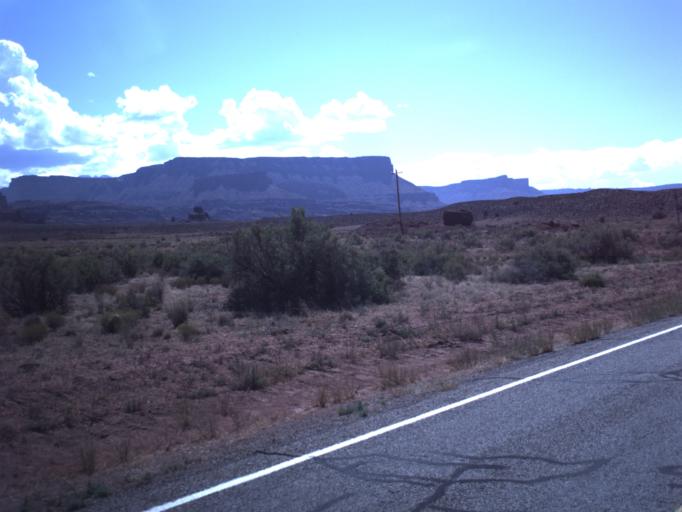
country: US
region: Utah
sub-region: Grand County
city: Moab
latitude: 38.7577
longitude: -109.3252
